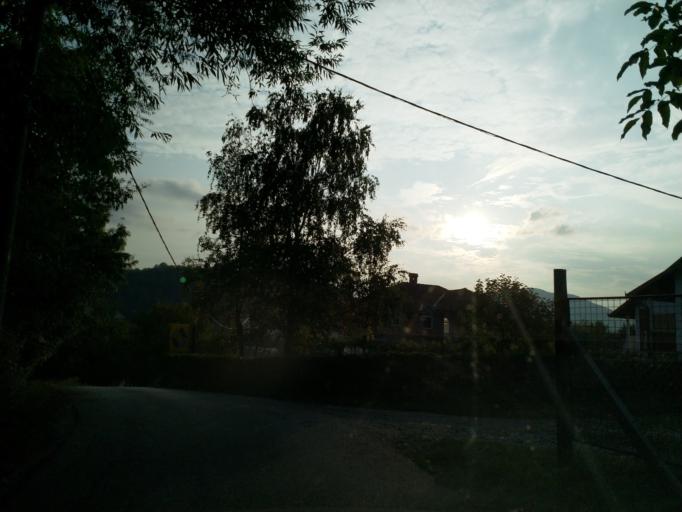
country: RS
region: Central Serbia
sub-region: Sumadijski Okrug
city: Arangelovac
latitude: 44.3043
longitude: 20.5881
